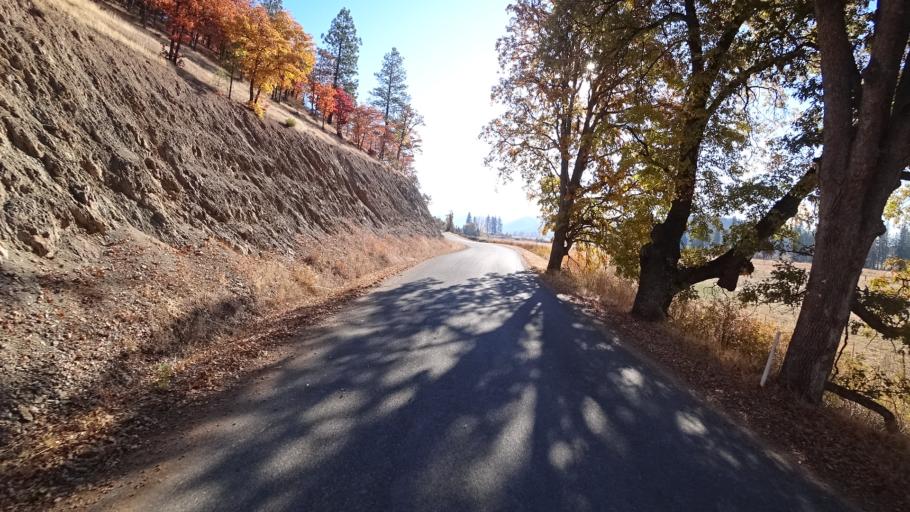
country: US
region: California
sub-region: Siskiyou County
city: Yreka
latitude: 41.6388
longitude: -122.9866
